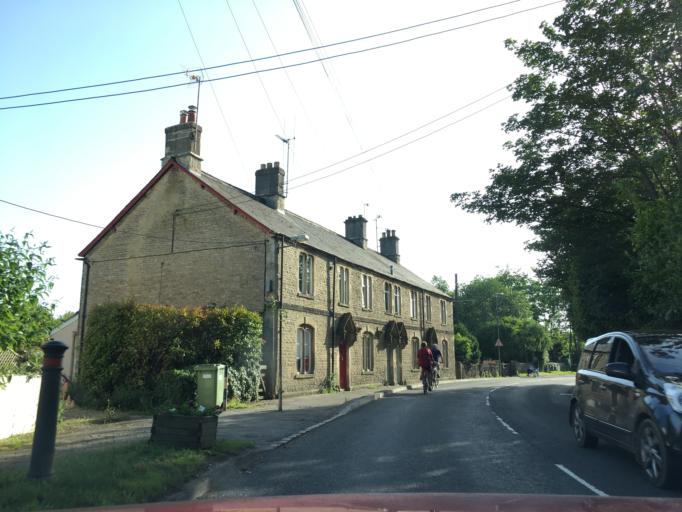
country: GB
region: England
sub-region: Gloucestershire
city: Fairford
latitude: 51.7070
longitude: -1.7764
